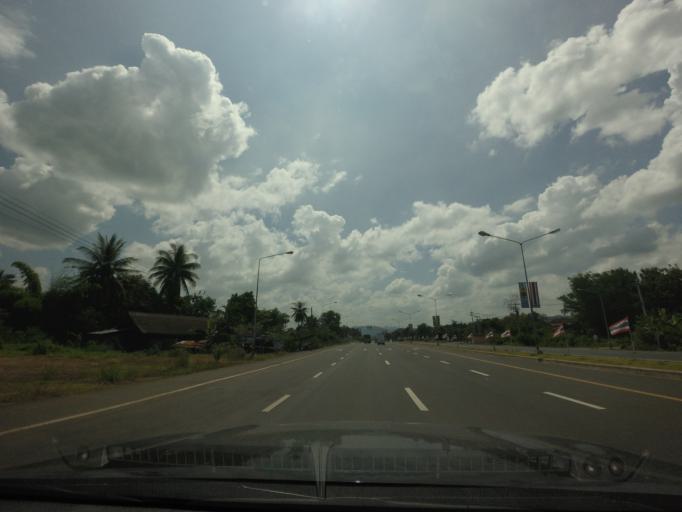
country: TH
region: Phetchabun
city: Phetchabun
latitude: 16.4422
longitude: 101.1081
